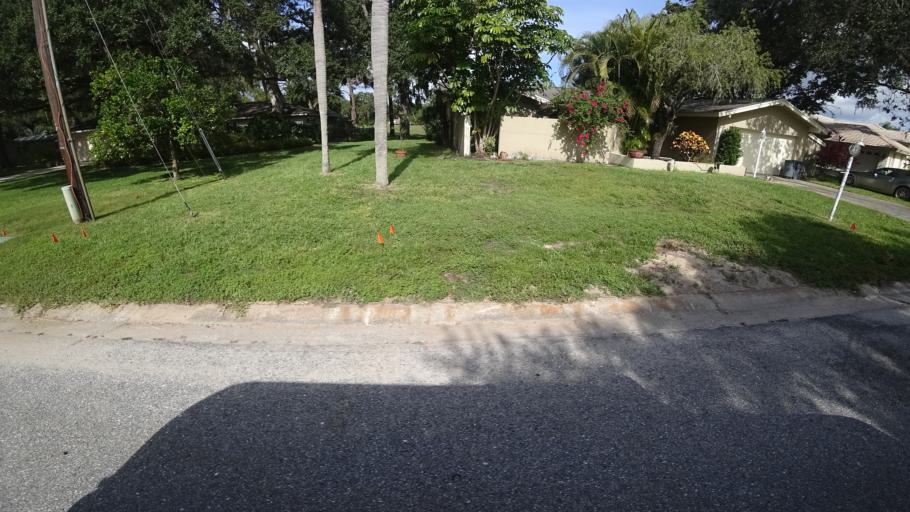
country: US
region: Florida
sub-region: Sarasota County
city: Desoto Lakes
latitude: 27.4039
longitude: -82.4985
